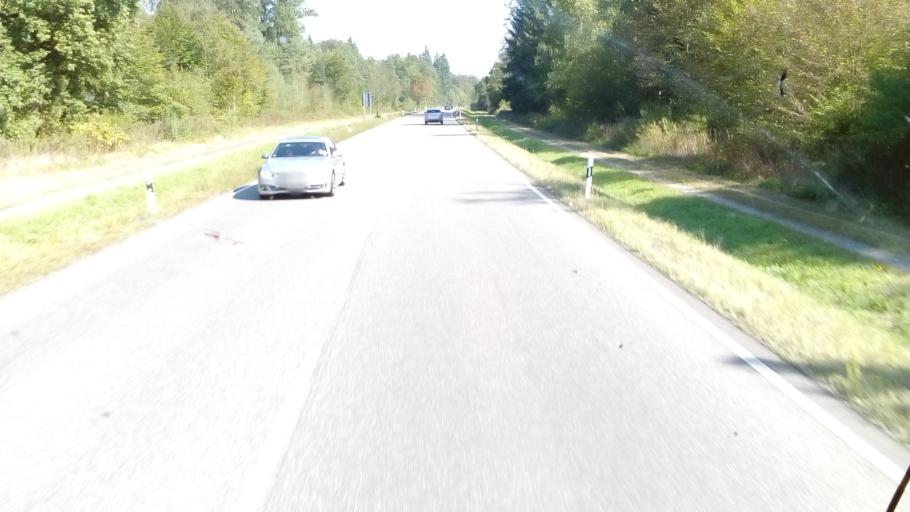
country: DE
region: Rheinland-Pfalz
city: Scheibenhardt
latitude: 48.9853
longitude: 8.1637
